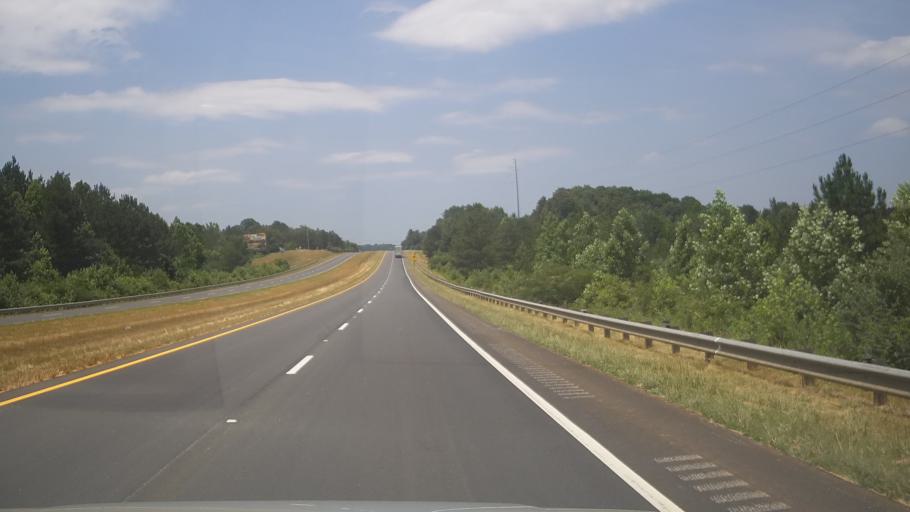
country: US
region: Georgia
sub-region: Jackson County
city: Commerce
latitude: 34.2092
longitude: -83.4387
